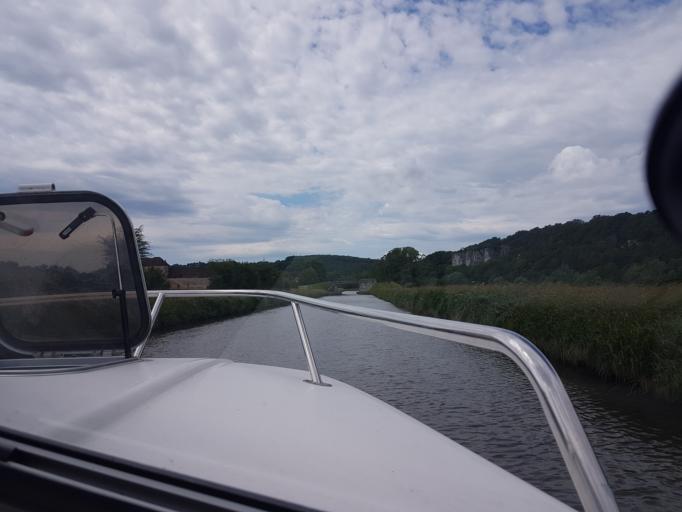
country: FR
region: Bourgogne
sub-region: Departement de la Nievre
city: Clamecy
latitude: 47.4997
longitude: 3.5162
